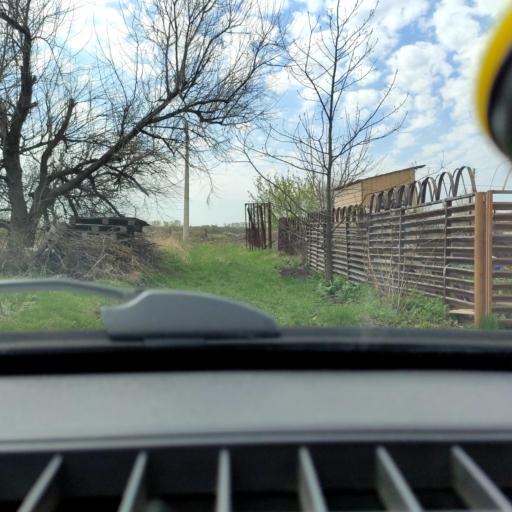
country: RU
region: Samara
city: Tol'yatti
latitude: 53.6968
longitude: 49.4545
